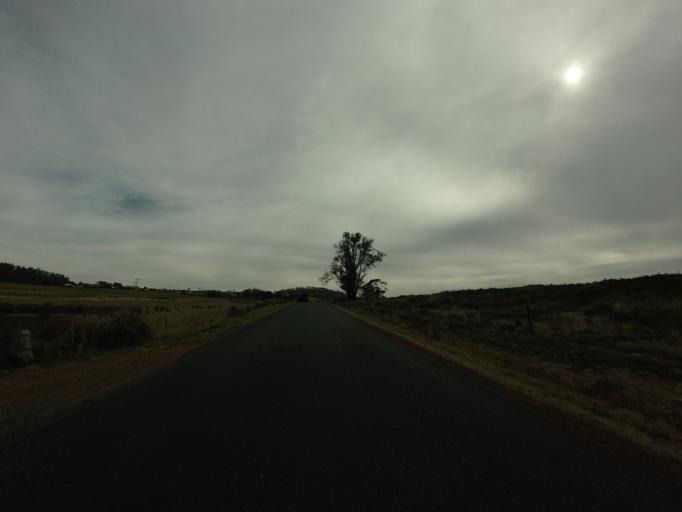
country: AU
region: Tasmania
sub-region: Sorell
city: Sorell
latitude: -42.4568
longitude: 147.5739
